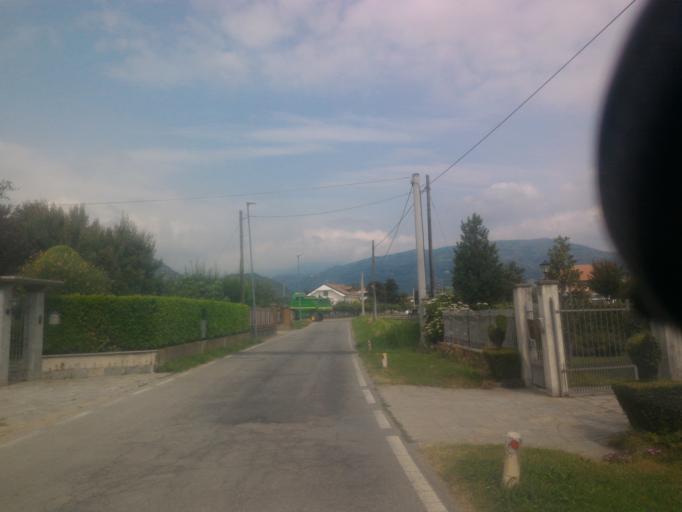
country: IT
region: Piedmont
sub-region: Provincia di Torino
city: Pinerolo
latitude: 44.8676
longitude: 7.3207
